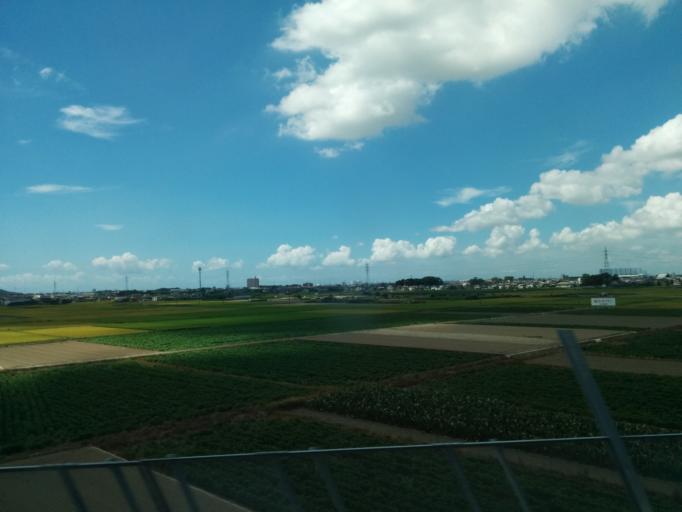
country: JP
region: Aichi
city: Anjo
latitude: 34.9197
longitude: 137.1060
